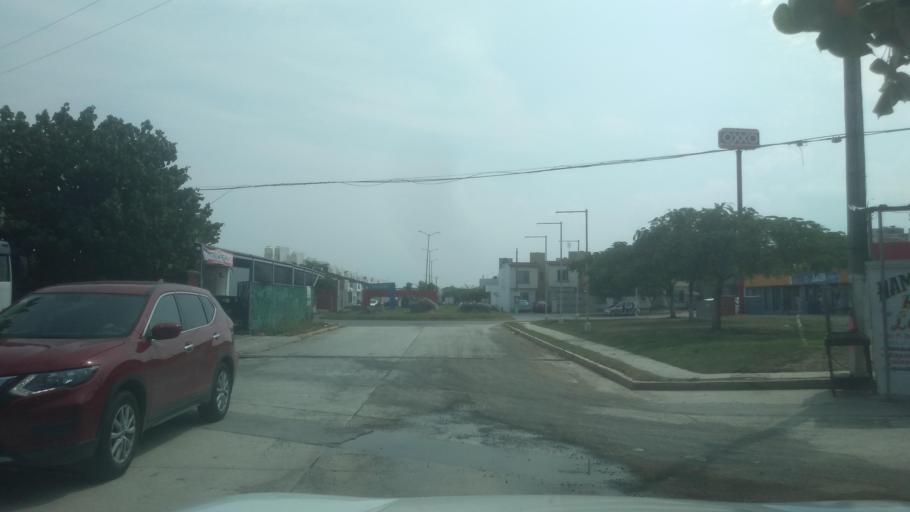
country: MX
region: Veracruz
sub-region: Veracruz
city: Las Amapolas
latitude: 19.1633
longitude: -96.1820
